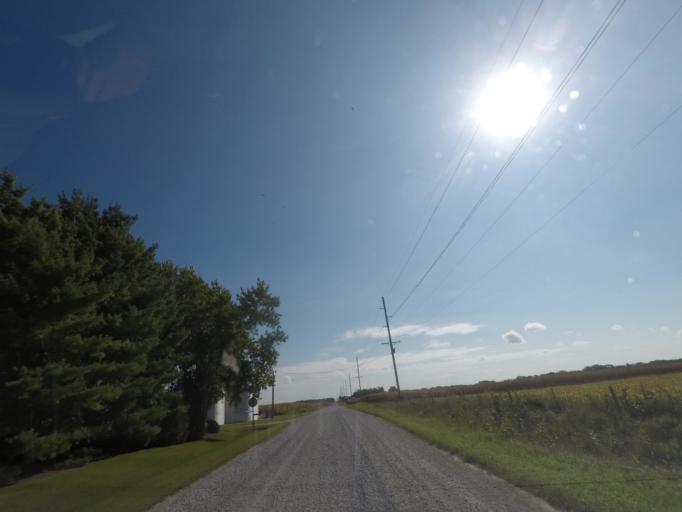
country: US
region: Iowa
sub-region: Story County
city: Nevada
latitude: 42.0343
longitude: -93.3921
